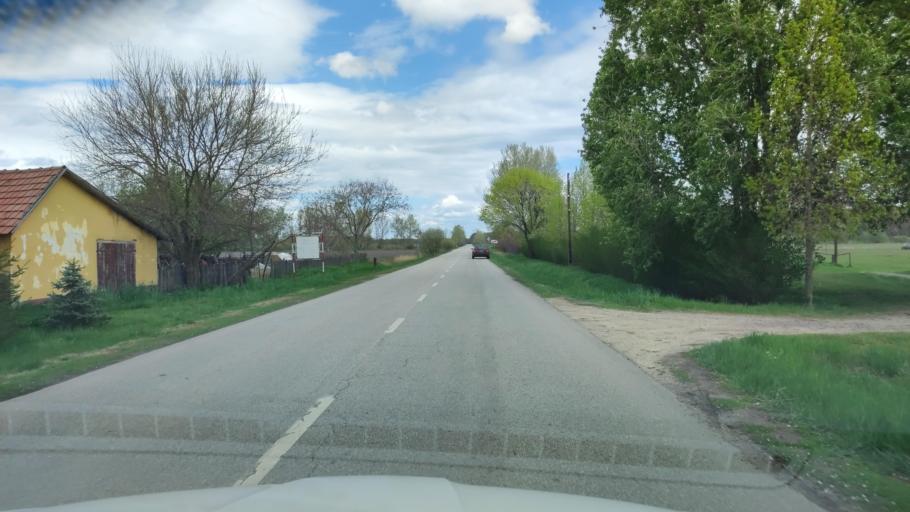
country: HU
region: Pest
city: Kocser
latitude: 47.0042
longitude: 19.9239
